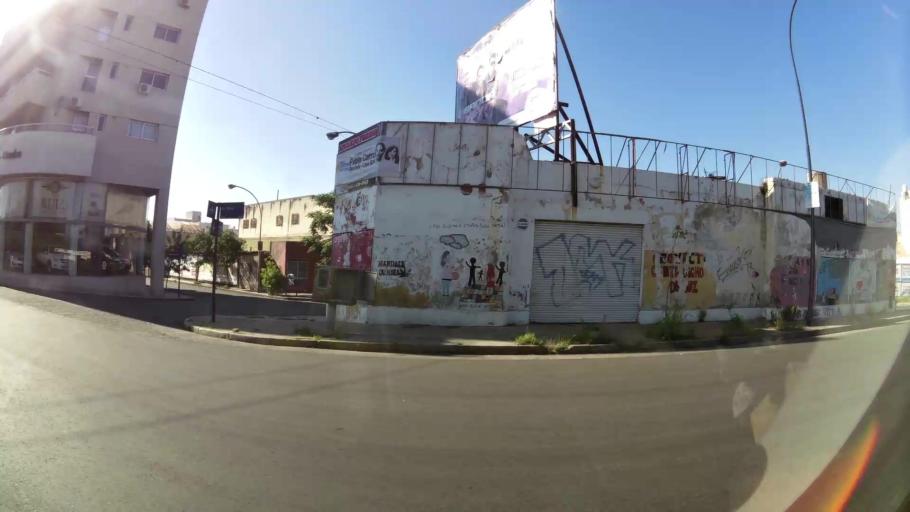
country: AR
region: Cordoba
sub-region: Departamento de Capital
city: Cordoba
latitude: -31.4064
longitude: -64.1819
